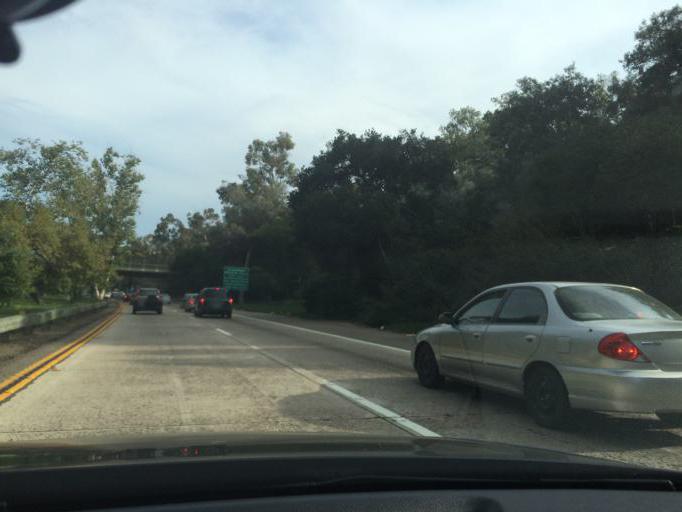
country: US
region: California
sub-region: San Diego County
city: San Diego
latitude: 32.7419
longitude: -117.1566
